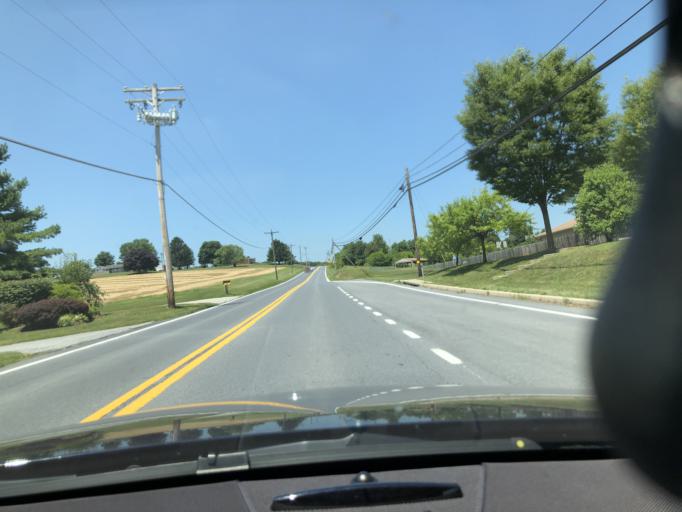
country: US
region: Maryland
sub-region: Carroll County
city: Westminster
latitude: 39.5169
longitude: -76.9808
